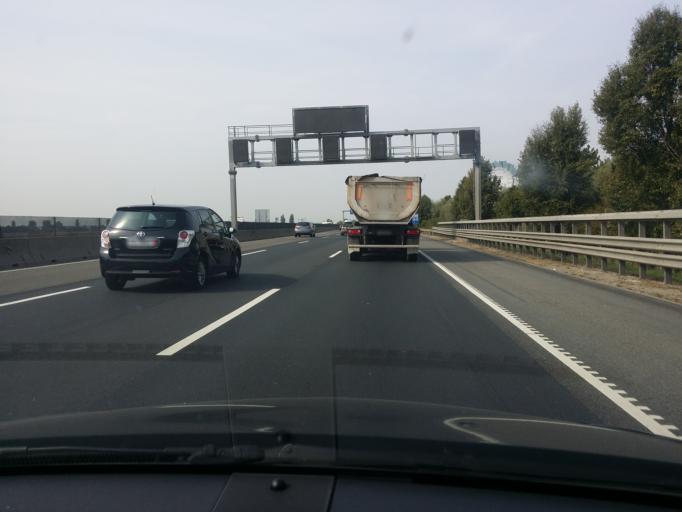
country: HU
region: Pest
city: Dunaharaszti
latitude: 47.3787
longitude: 19.0666
